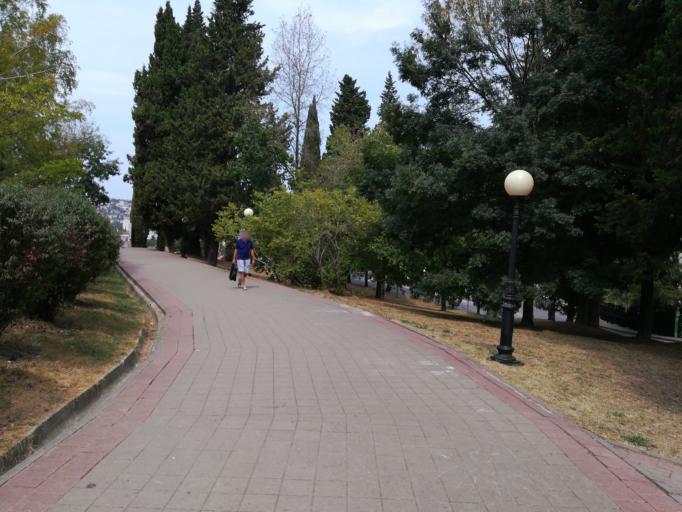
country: RU
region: Krasnodarskiy
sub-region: Sochi City
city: Sochi
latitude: 43.5889
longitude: 39.7313
